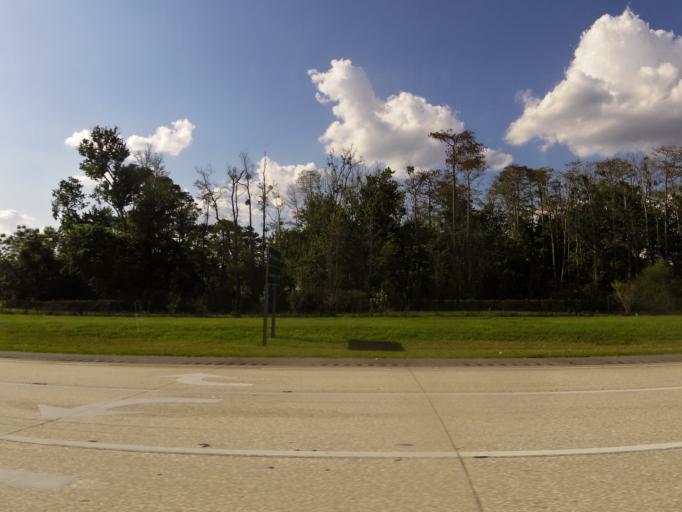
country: US
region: Florida
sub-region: Saint Johns County
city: Palm Valley
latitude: 30.1384
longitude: -81.5102
